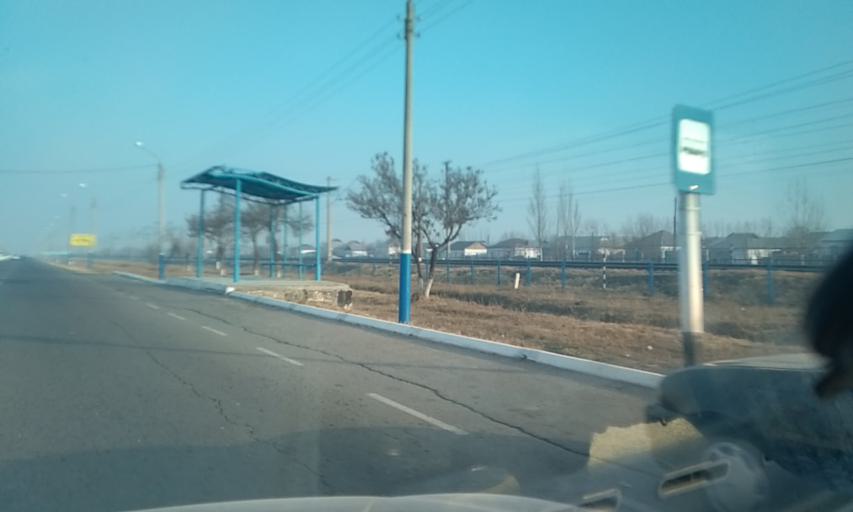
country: UZ
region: Sirdaryo
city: Guliston
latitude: 40.5422
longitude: 68.7502
